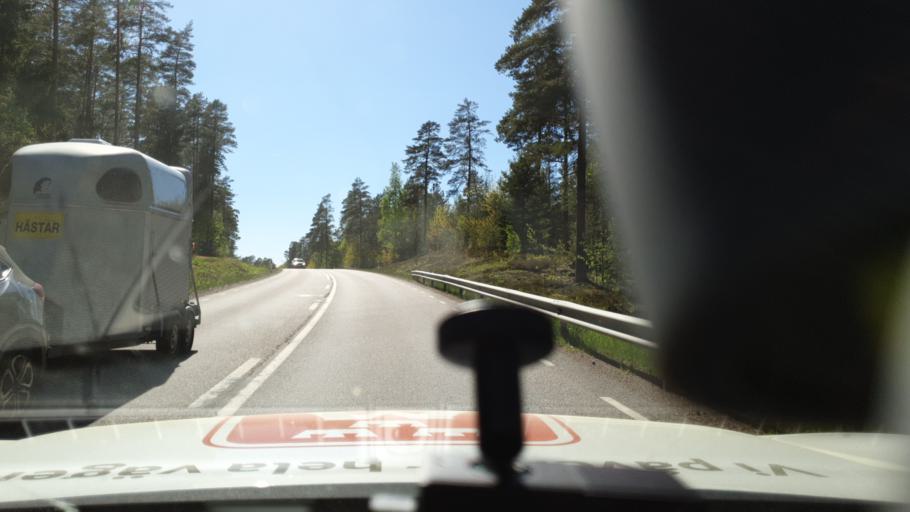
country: SE
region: Kalmar
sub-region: Hultsfreds Kommun
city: Virserum
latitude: 57.4067
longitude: 15.5163
